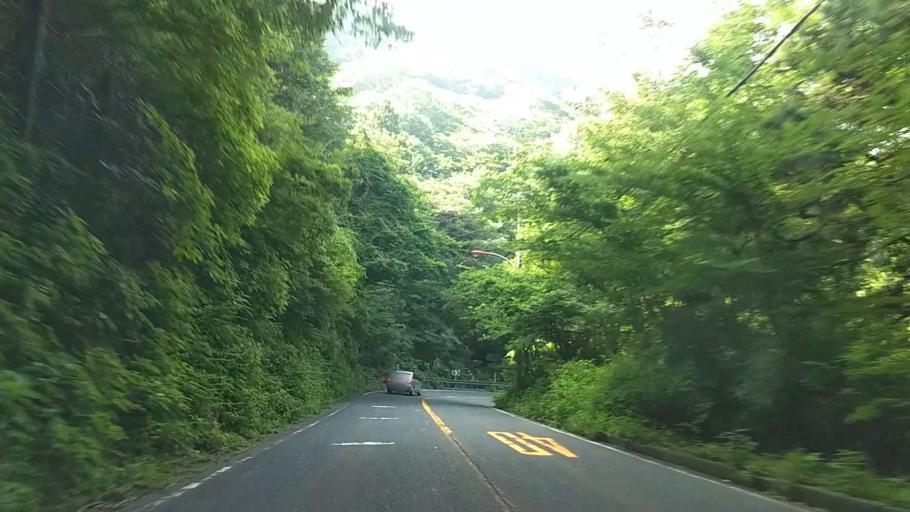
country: JP
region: Kanagawa
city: Hakone
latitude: 35.2236
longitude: 139.0474
